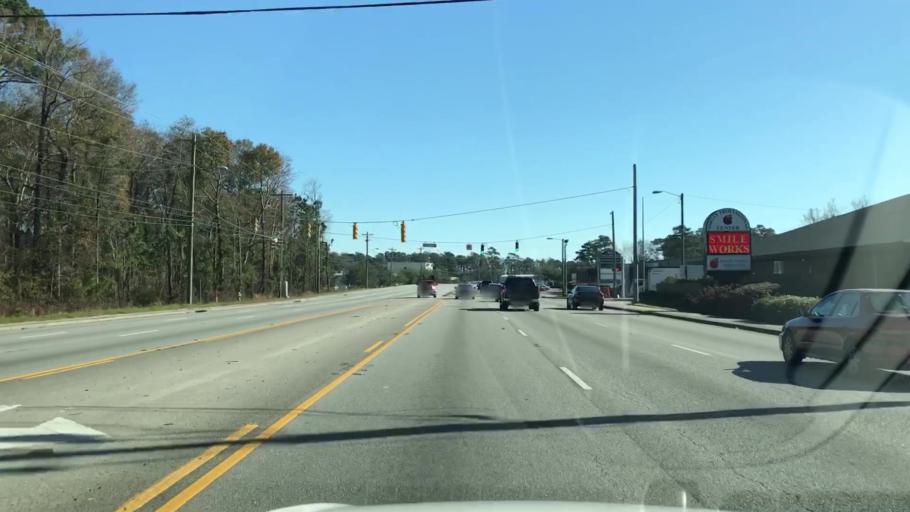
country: US
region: South Carolina
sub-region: Berkeley County
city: Hanahan
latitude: 32.9307
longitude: -80.0670
